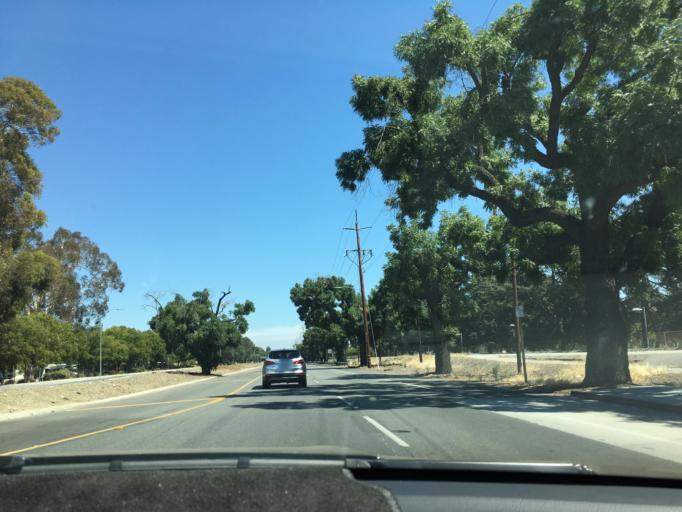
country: US
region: California
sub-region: Santa Clara County
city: Seven Trees
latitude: 37.2524
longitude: -121.7972
